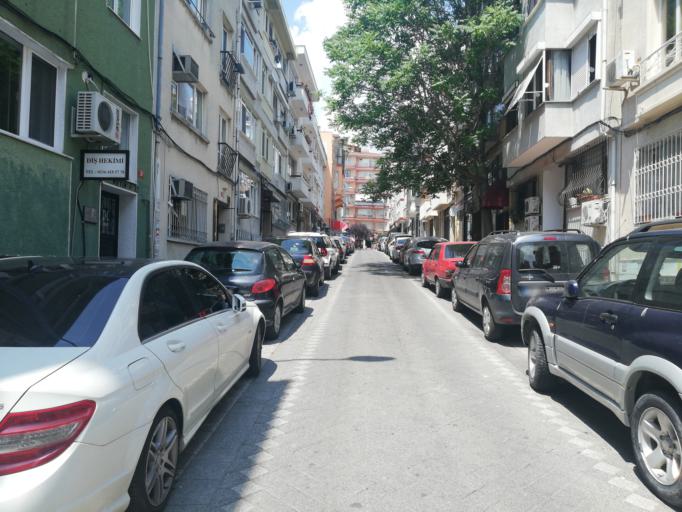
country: TR
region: Istanbul
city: UEskuedar
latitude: 40.9851
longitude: 29.0289
